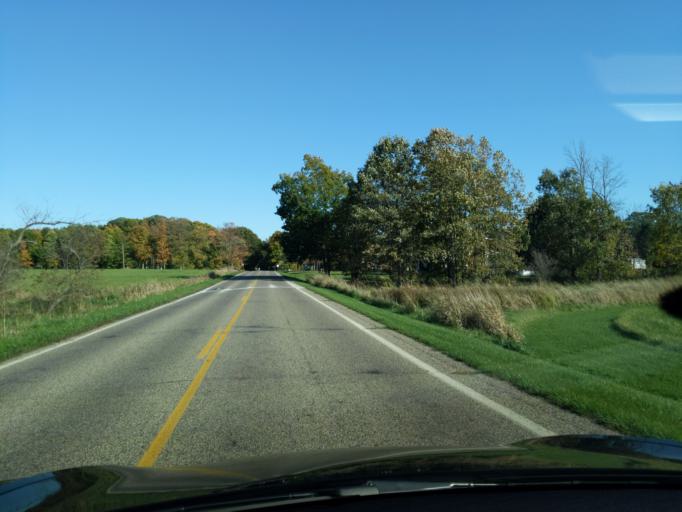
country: US
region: Michigan
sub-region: Shiawassee County
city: Laingsburg
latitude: 42.9292
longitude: -84.4274
